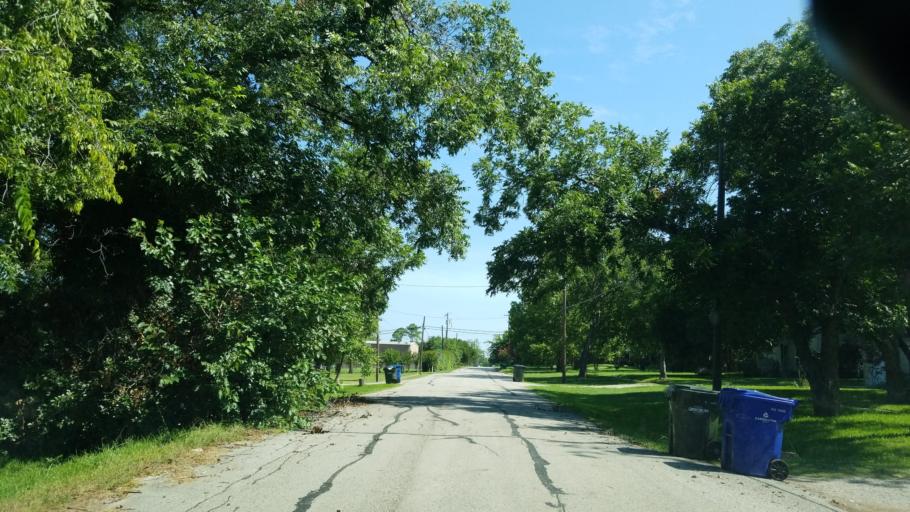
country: US
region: Texas
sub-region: Dallas County
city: Carrollton
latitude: 32.9617
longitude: -96.9121
